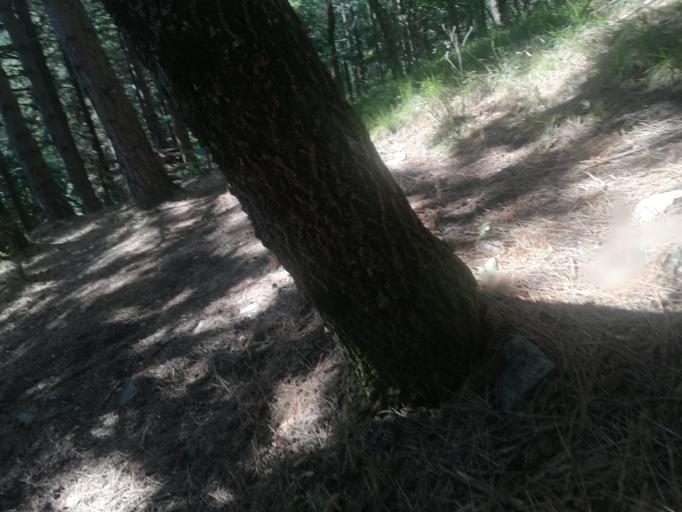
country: IT
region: Apulia
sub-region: Provincia di Foggia
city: Biccari
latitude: 41.3721
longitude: 15.1705
